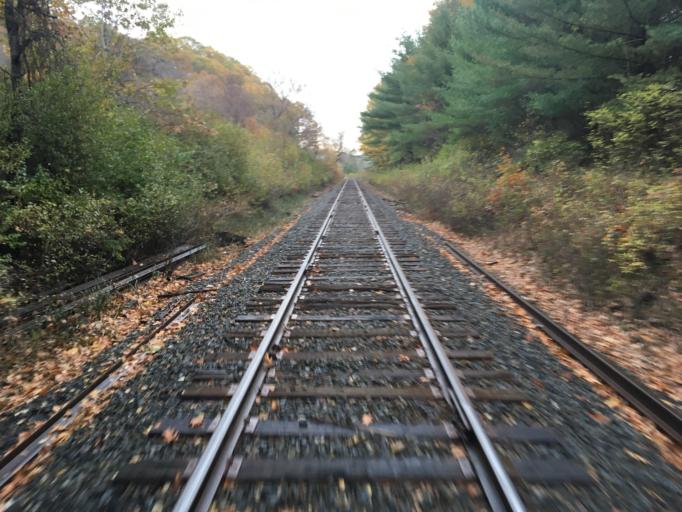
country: US
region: New Hampshire
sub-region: Grafton County
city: Hanover
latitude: 43.7167
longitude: -72.2884
